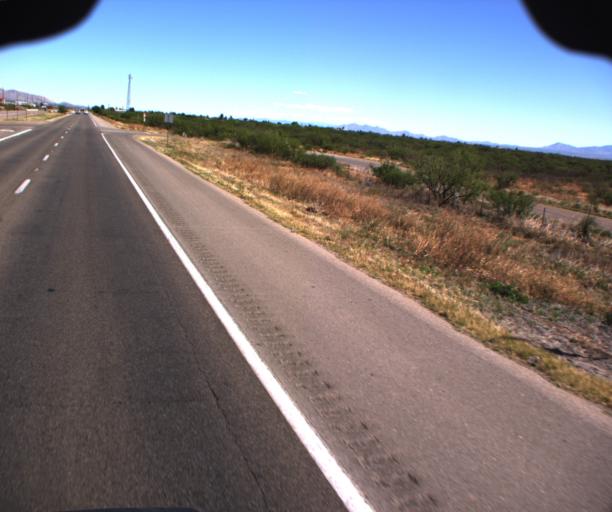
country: US
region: Arizona
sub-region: Cochise County
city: Huachuca City
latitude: 31.6755
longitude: -110.3501
